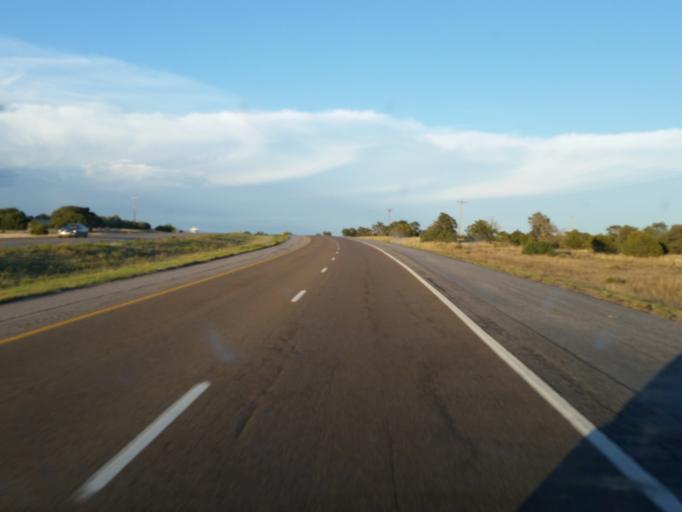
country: US
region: New Mexico
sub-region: Torrance County
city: Moriarty
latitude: 35.0019
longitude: -105.5532
